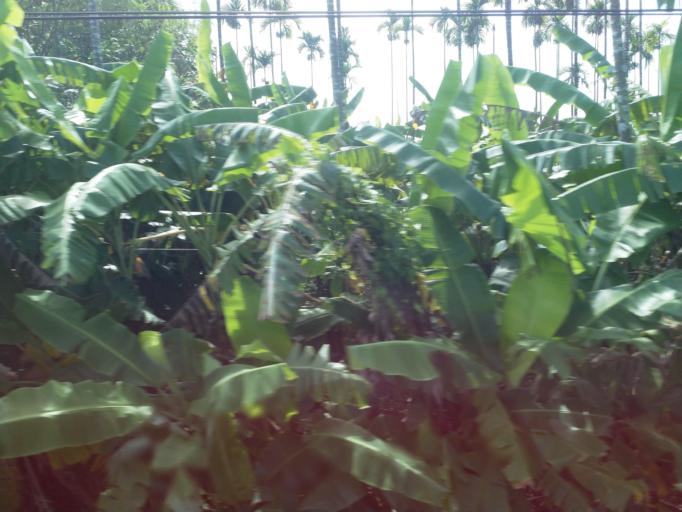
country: TW
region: Taiwan
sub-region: Pingtung
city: Pingtung
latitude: 22.8899
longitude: 120.5063
